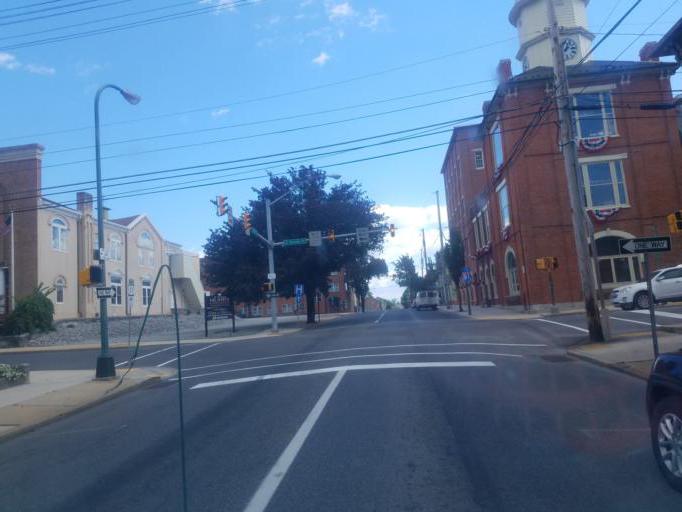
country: US
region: Pennsylvania
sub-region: Franklin County
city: Chambersburg
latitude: 39.9357
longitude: -77.6598
